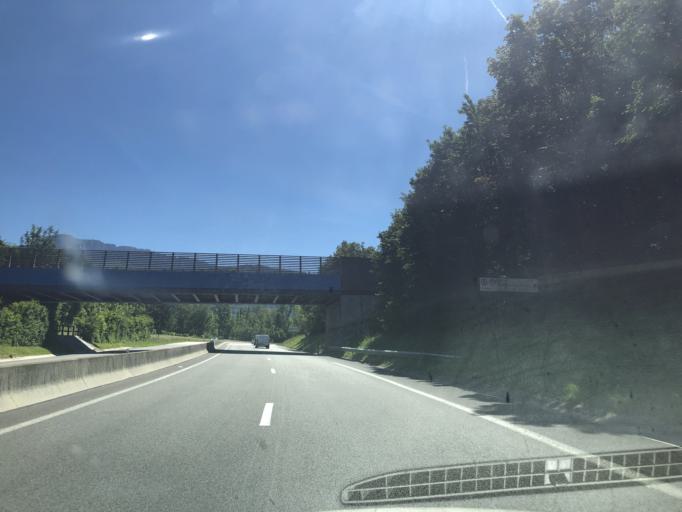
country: FR
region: Rhone-Alpes
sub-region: Departement de la Haute-Savoie
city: Villaz
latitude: 45.9357
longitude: 6.1664
